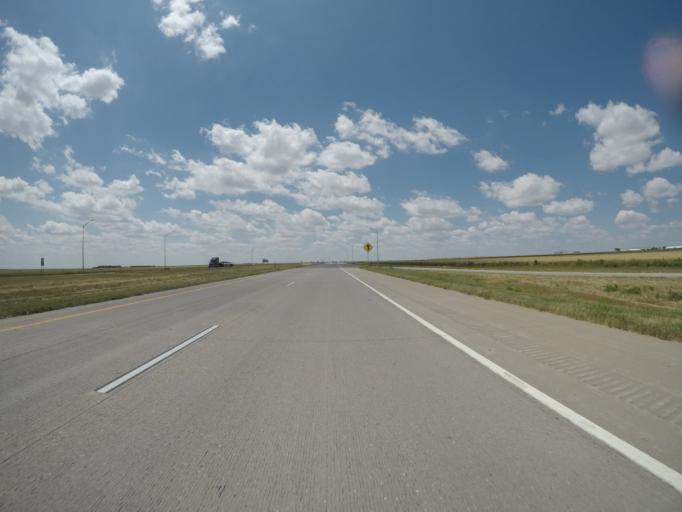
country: US
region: Colorado
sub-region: Kit Carson County
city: Burlington
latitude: 39.2943
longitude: -102.2811
